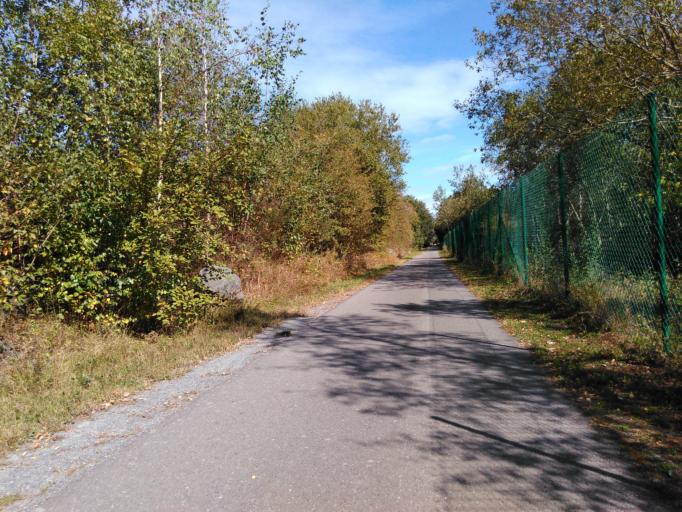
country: BE
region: Wallonia
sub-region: Province du Luxembourg
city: Bastogne
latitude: 50.0142
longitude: 5.7375
